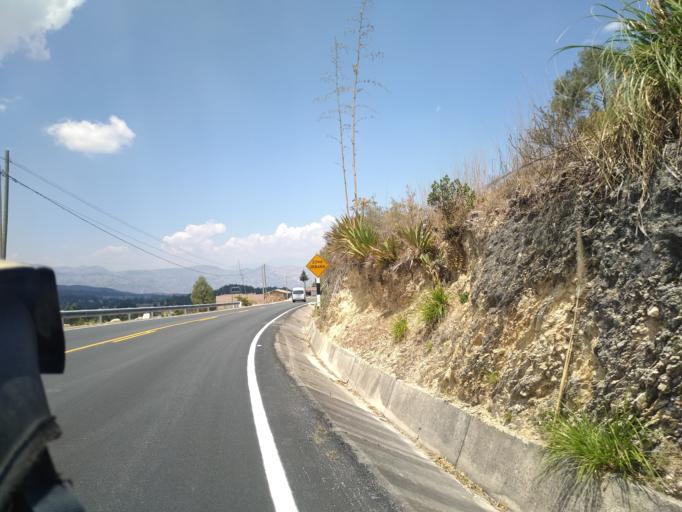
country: PE
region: Cajamarca
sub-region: San Marcos
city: San Marcos
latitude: -7.2763
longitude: -78.2434
